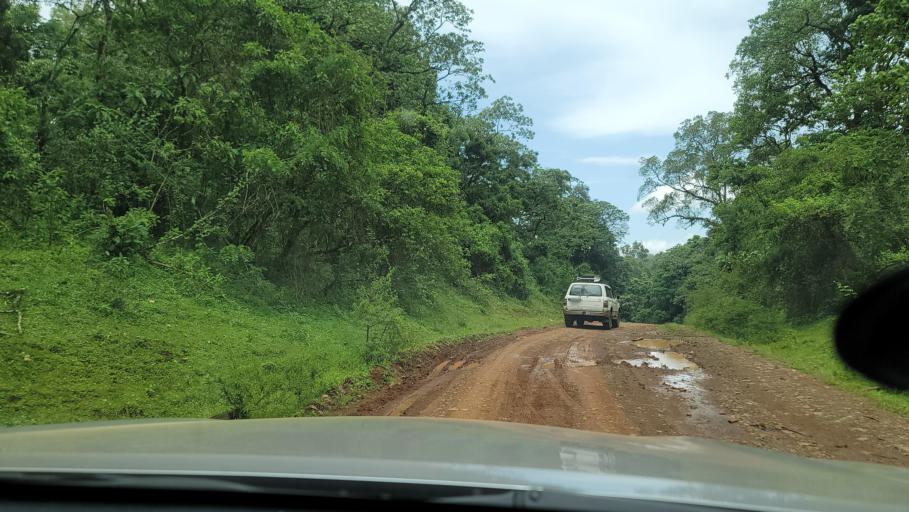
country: ET
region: Southern Nations, Nationalities, and People's Region
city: Bonga
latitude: 7.6746
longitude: 36.2431
